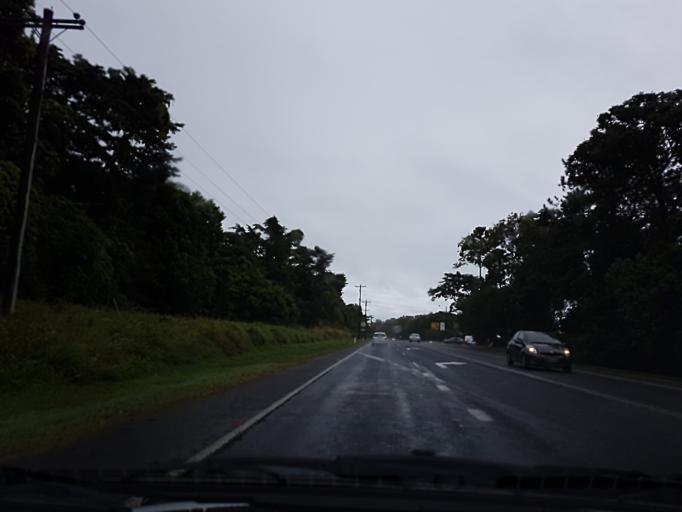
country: AU
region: Queensland
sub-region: Cairns
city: Palm Cove
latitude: -16.7491
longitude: 145.6625
